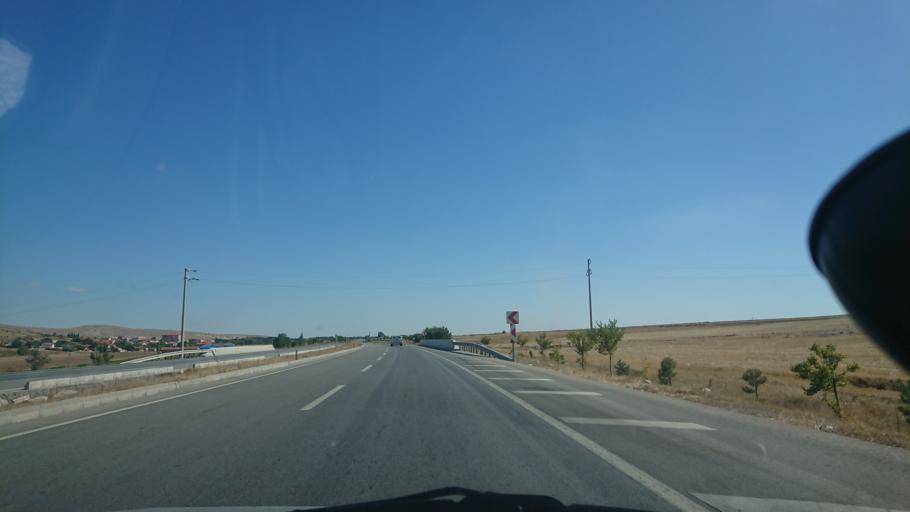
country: TR
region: Eskisehir
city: Mahmudiye
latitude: 39.4973
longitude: 30.9709
